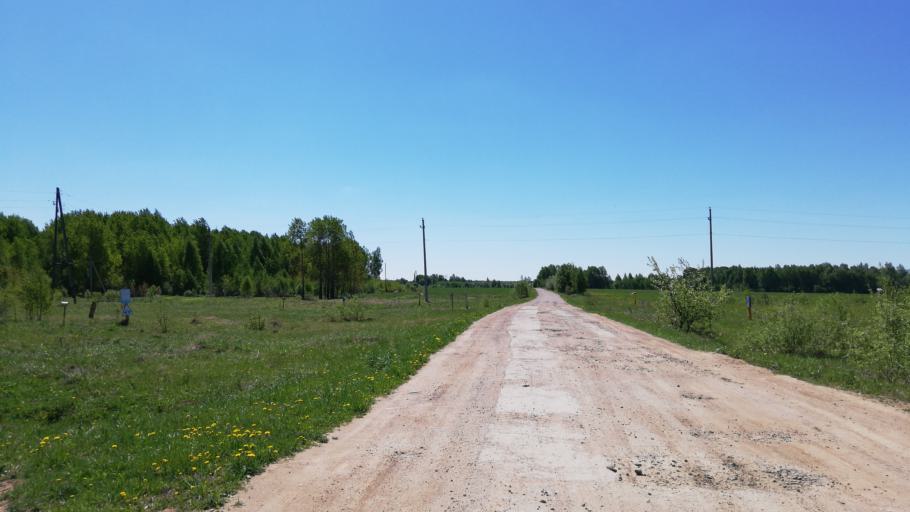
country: RU
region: Ivanovo
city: Pistsovo
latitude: 57.1249
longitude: 40.6008
